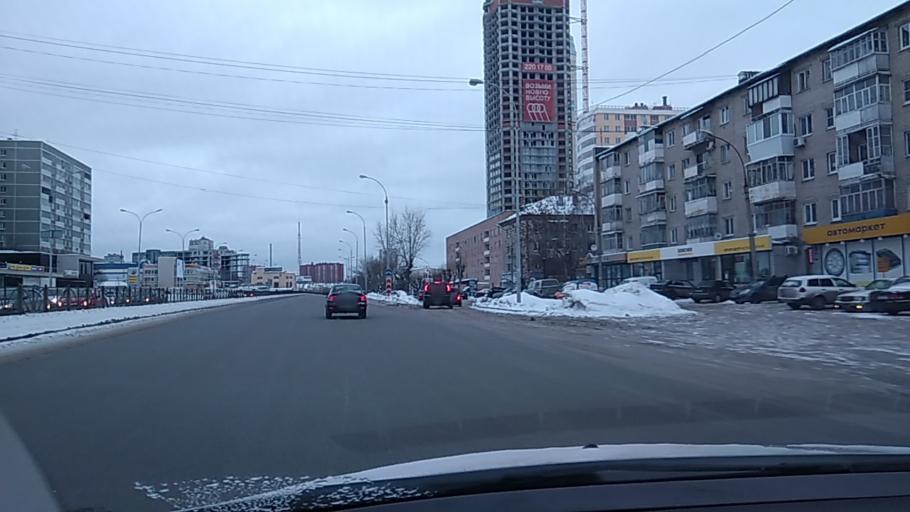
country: RU
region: Sverdlovsk
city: Yekaterinburg
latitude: 56.8108
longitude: 60.6299
